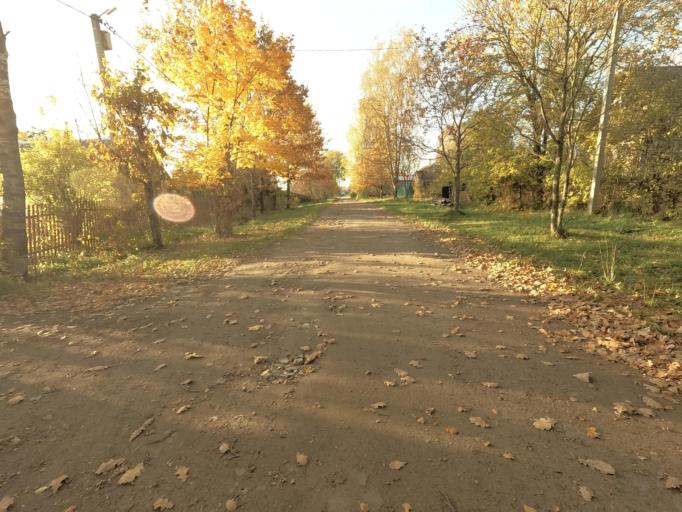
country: RU
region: Leningrad
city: Mga
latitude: 59.7529
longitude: 31.0551
